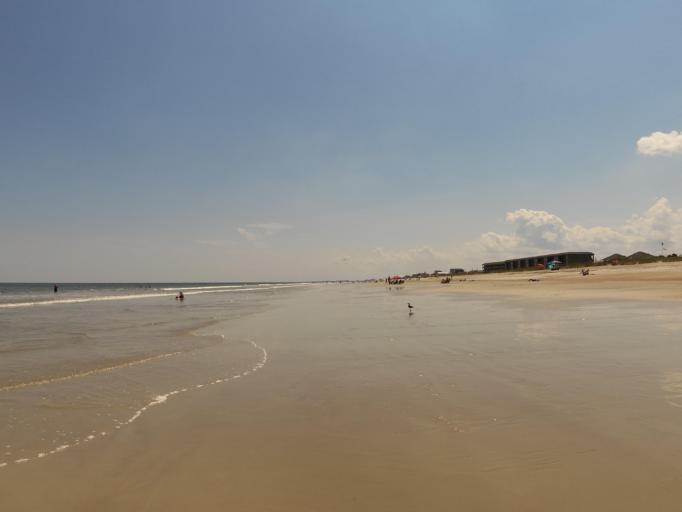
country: US
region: Florida
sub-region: Nassau County
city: Fernandina Beach
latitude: 30.6648
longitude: -81.4302
